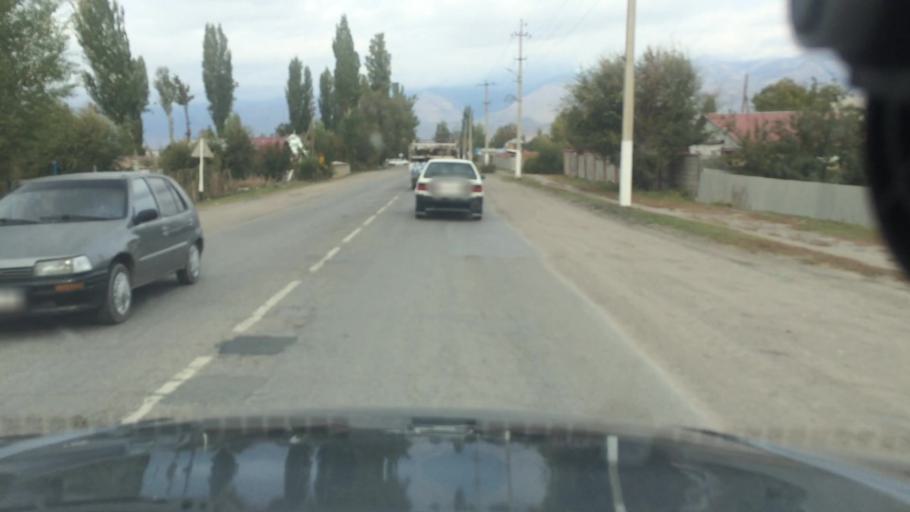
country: KG
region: Ysyk-Koel
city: Tyup
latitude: 42.7241
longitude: 78.3653
